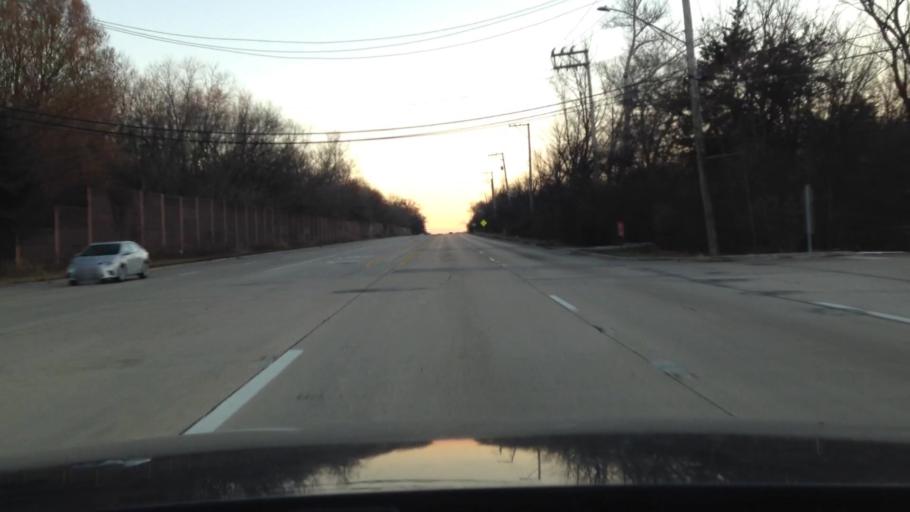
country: US
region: Illinois
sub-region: Cook County
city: Bartlett
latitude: 41.9913
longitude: -88.2075
